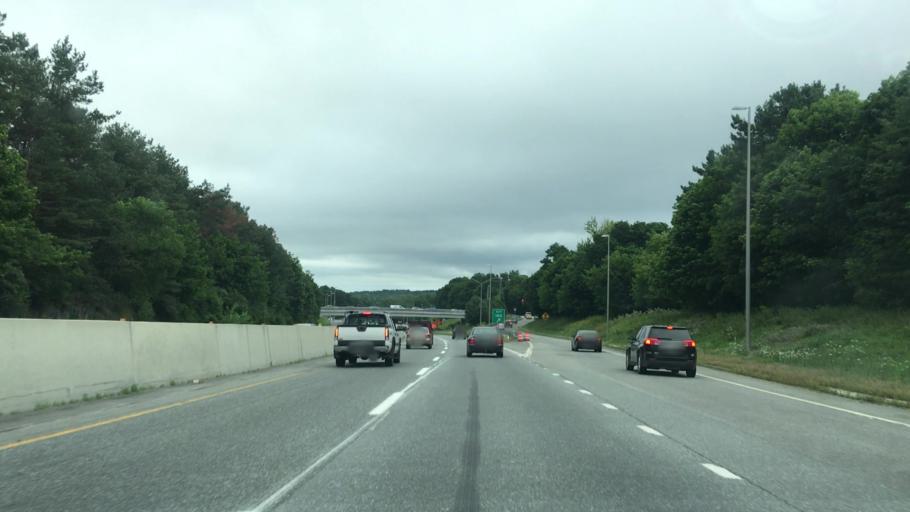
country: US
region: Maine
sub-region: Penobscot County
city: Bangor
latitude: 44.8065
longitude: -68.7956
